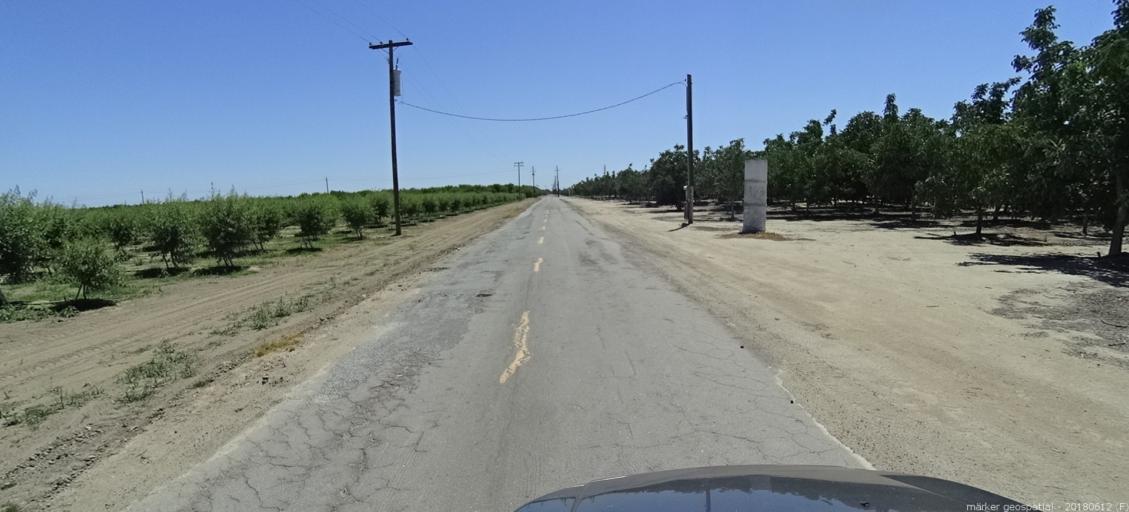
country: US
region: California
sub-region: Madera County
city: Chowchilla
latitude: 37.0616
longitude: -120.3317
